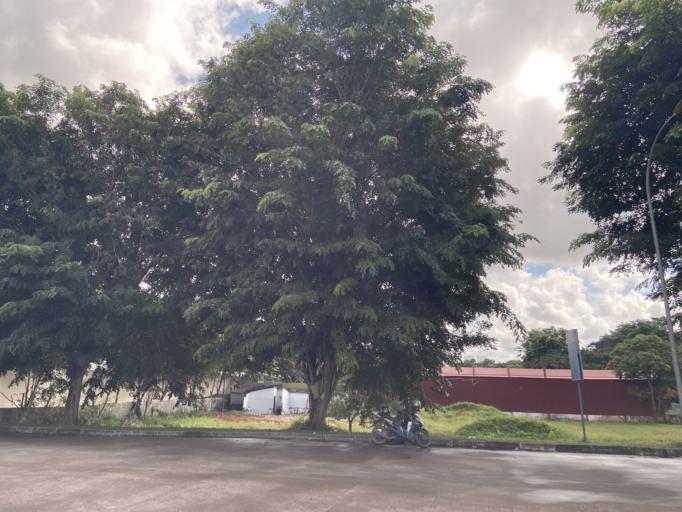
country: SG
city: Singapore
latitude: 1.0964
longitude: 104.0361
